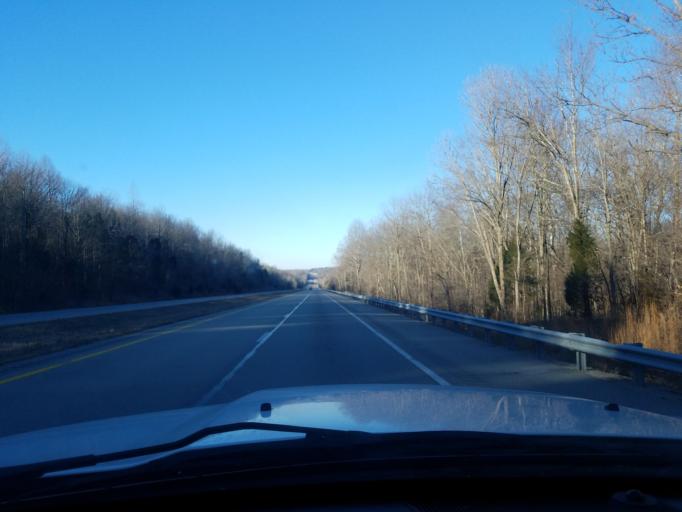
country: US
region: Kentucky
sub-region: Ohio County
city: Oak Grove
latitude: 37.3950
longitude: -86.5784
